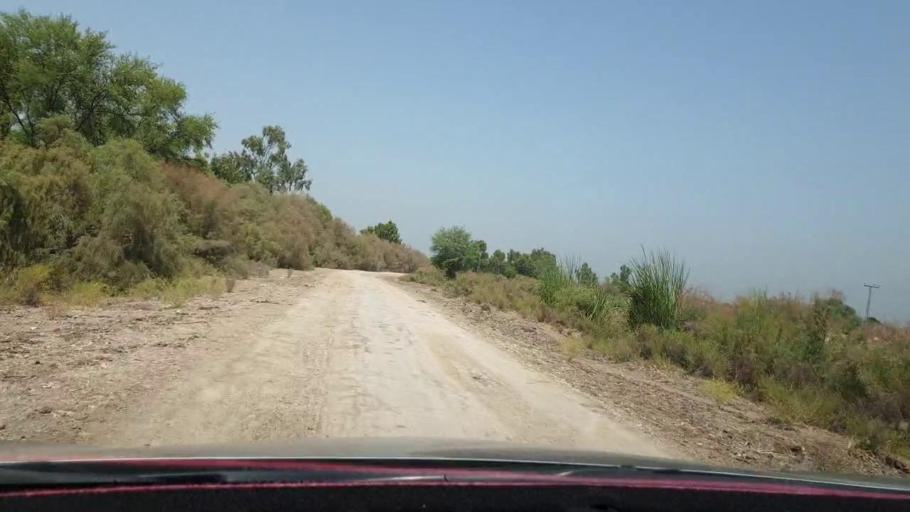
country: PK
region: Sindh
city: Warah
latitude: 27.4286
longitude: 67.6988
